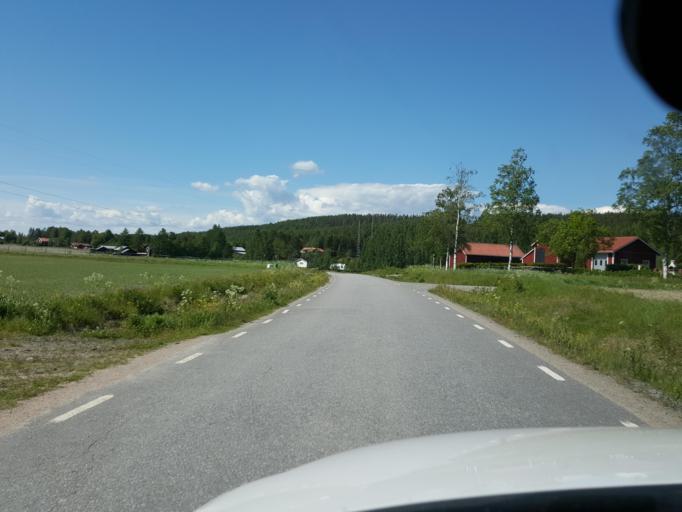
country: SE
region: Gaevleborg
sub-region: Ljusdals Kommun
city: Jaervsoe
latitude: 61.7444
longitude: 16.2705
